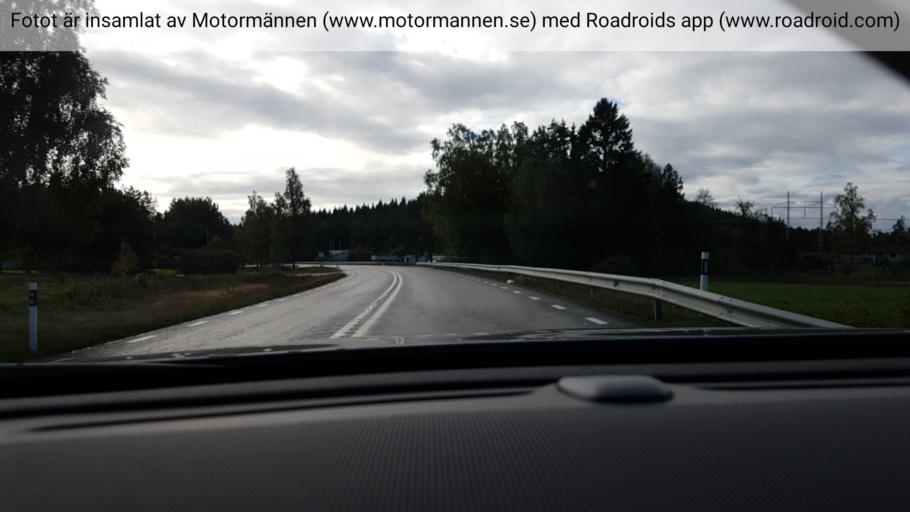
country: SE
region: Vaestra Goetaland
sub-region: Harryda Kommun
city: Ravlanda
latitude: 57.6062
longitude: 12.4377
